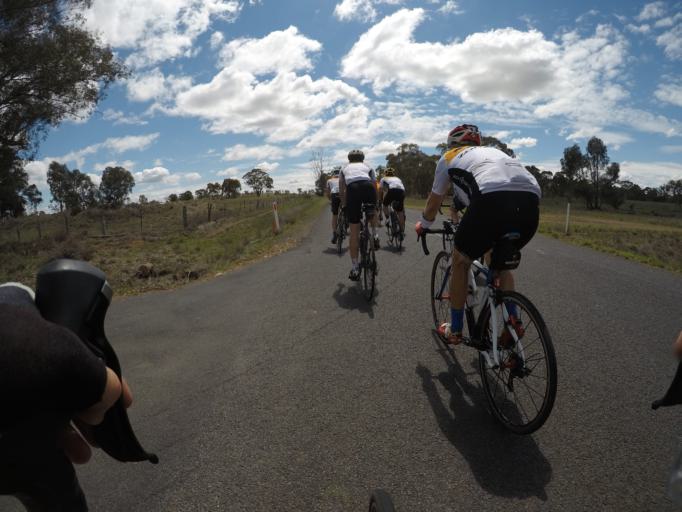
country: AU
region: New South Wales
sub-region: Dubbo Municipality
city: Dubbo
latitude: -32.3881
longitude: 148.5718
